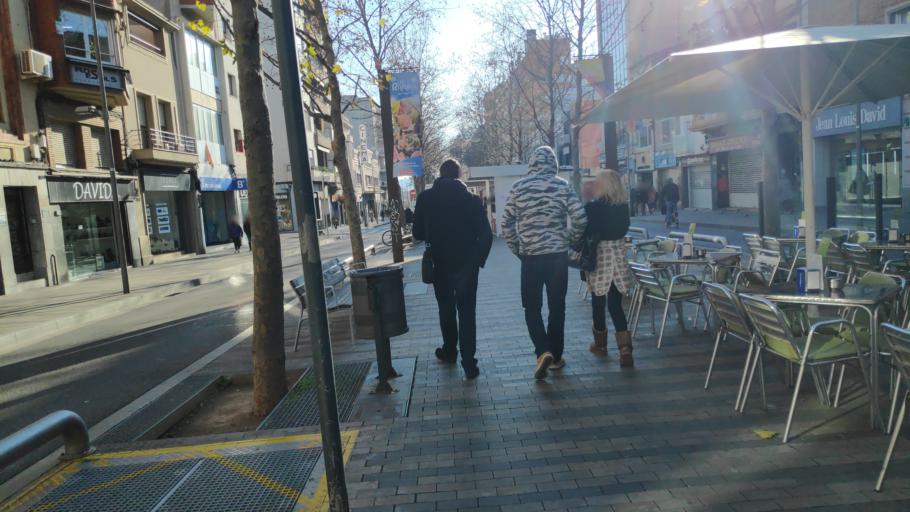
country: ES
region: Catalonia
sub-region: Provincia de Barcelona
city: Terrassa
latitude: 41.5623
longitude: 2.0078
